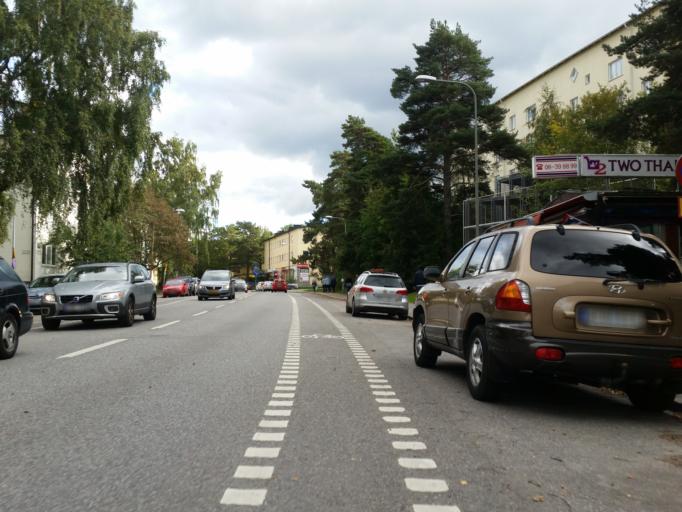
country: SE
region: Stockholm
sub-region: Stockholms Kommun
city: Arsta
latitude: 59.2976
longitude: 18.0907
